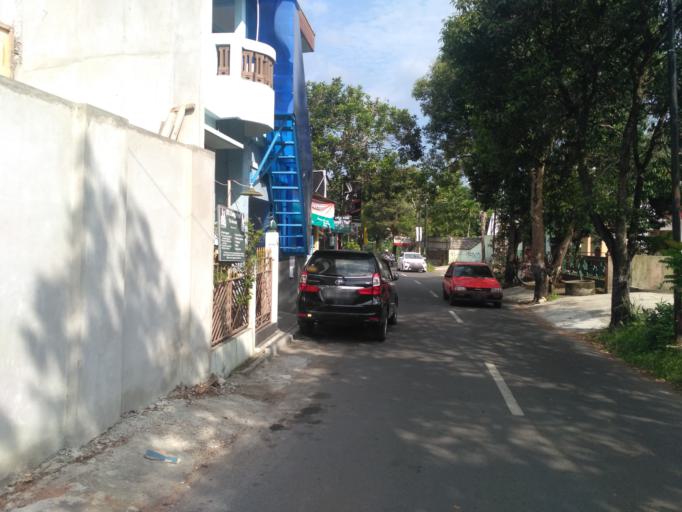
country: ID
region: Daerah Istimewa Yogyakarta
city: Depok
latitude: -7.7779
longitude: 110.4054
